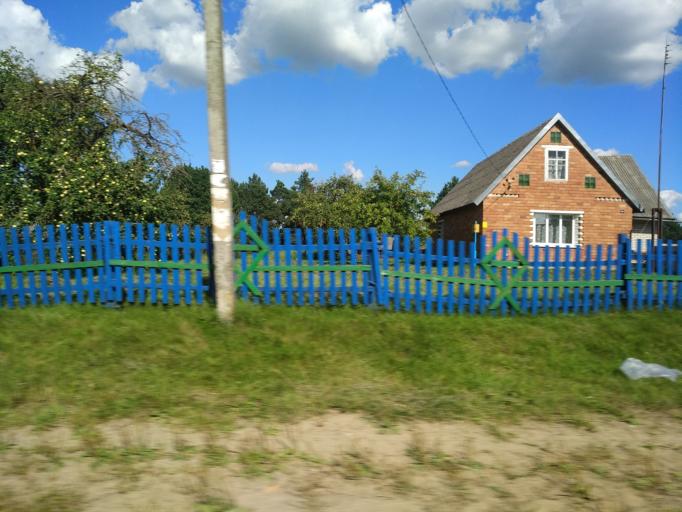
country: BY
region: Vitebsk
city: Mosar
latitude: 55.1265
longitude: 27.2101
